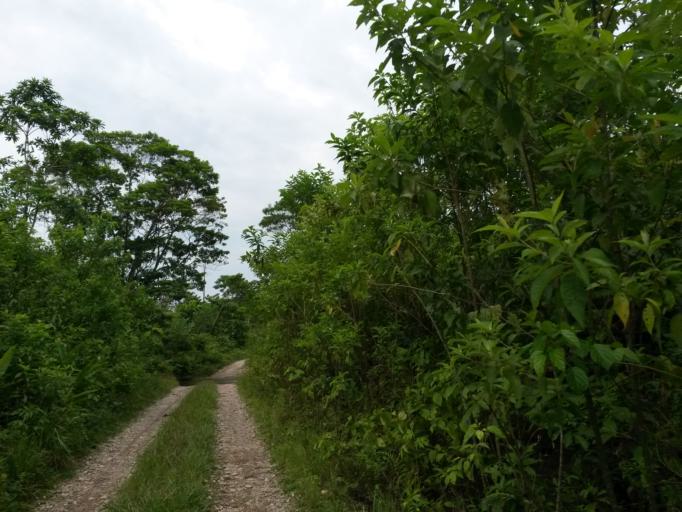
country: CO
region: Putumayo
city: Puerto Guzman
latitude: 1.0191
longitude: -76.3707
